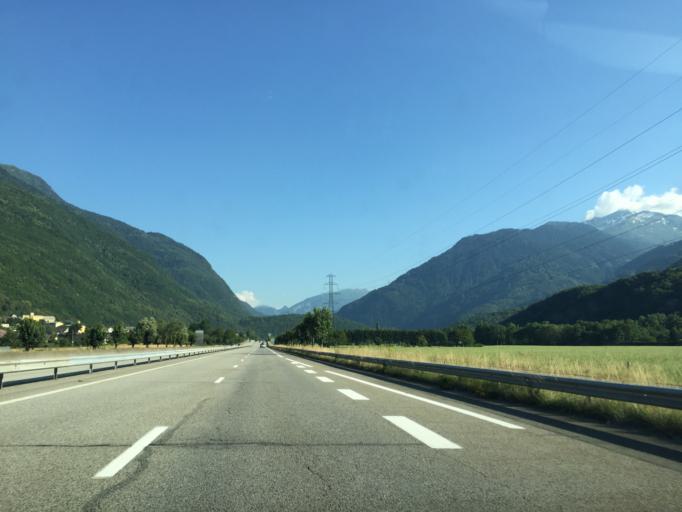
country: FR
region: Rhone-Alpes
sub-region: Departement de la Savoie
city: La Bathie
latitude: 45.6251
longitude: 6.4458
